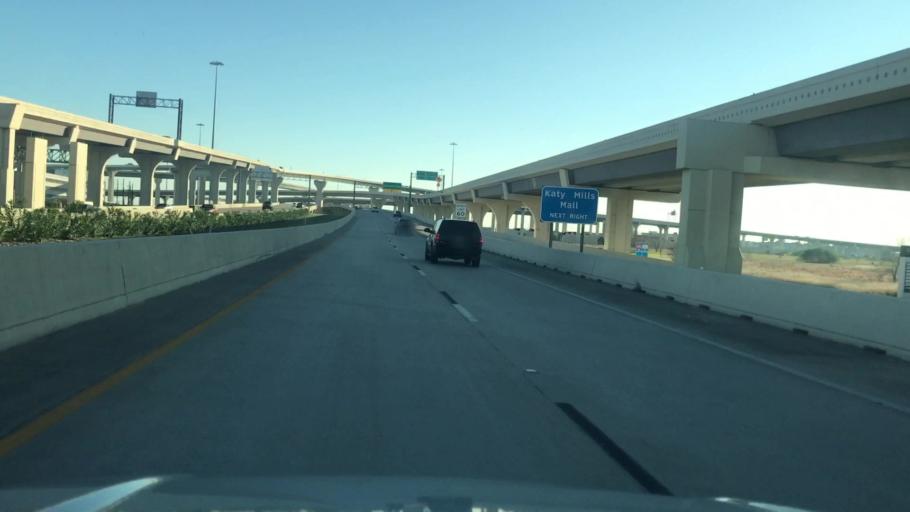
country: US
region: Texas
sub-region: Harris County
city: Katy
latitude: 29.7908
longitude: -95.7770
